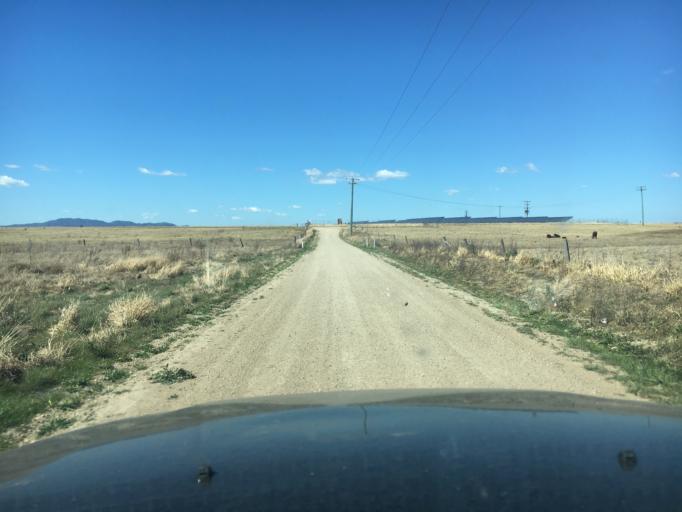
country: AU
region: New South Wales
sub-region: Singleton
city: Singleton
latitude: -32.5915
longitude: 151.1778
